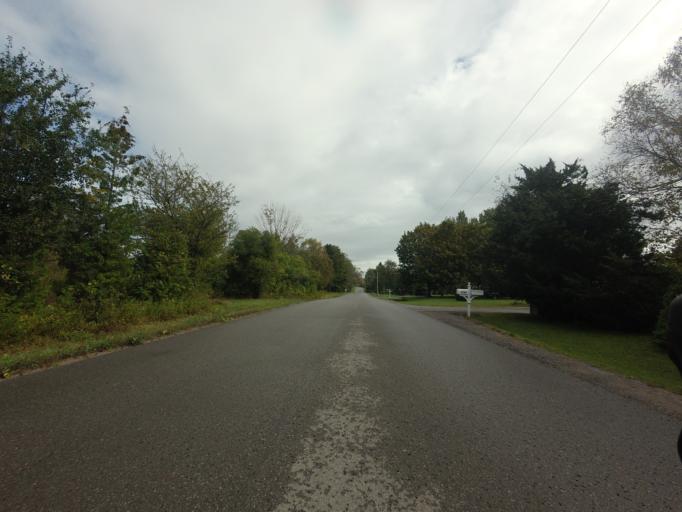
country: CA
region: Ontario
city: Cobourg
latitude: 43.9191
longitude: -78.4328
